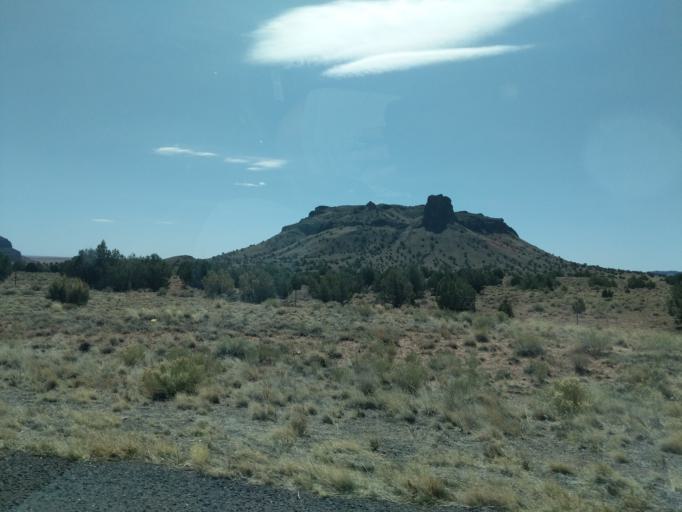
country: US
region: Arizona
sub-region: Navajo County
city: Dilkon
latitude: 35.3915
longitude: -110.0918
